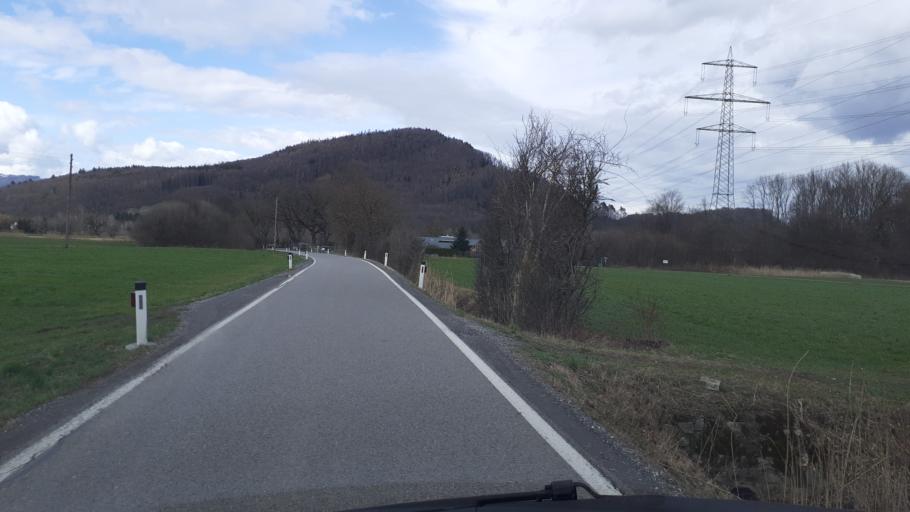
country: AT
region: Vorarlberg
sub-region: Politischer Bezirk Feldkirch
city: Koblach
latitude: 47.3209
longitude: 9.6162
